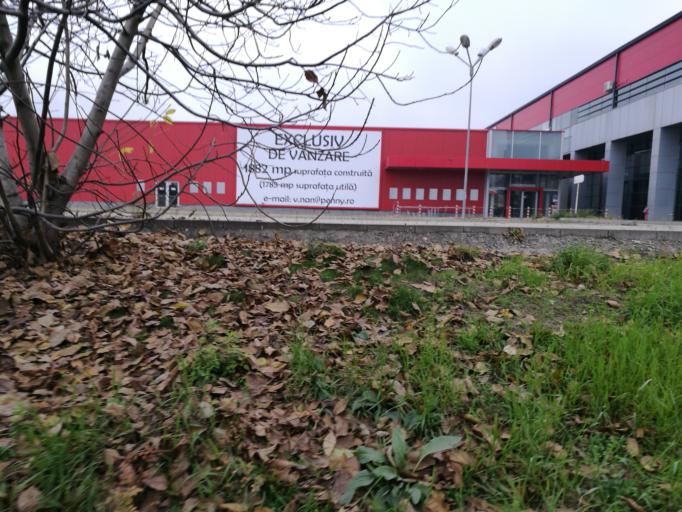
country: RO
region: Suceava
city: Suceava
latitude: 47.6704
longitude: 26.2764
